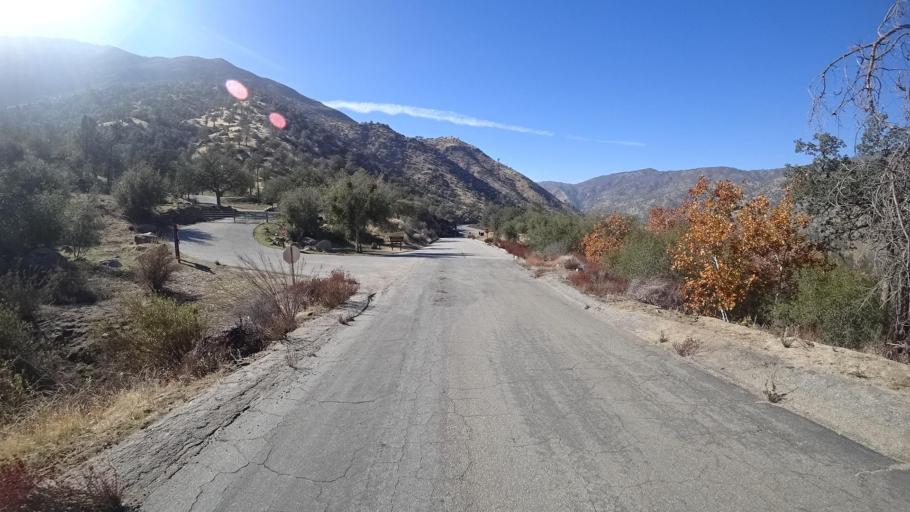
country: US
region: California
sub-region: Kern County
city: Bodfish
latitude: 35.5340
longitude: -118.6327
